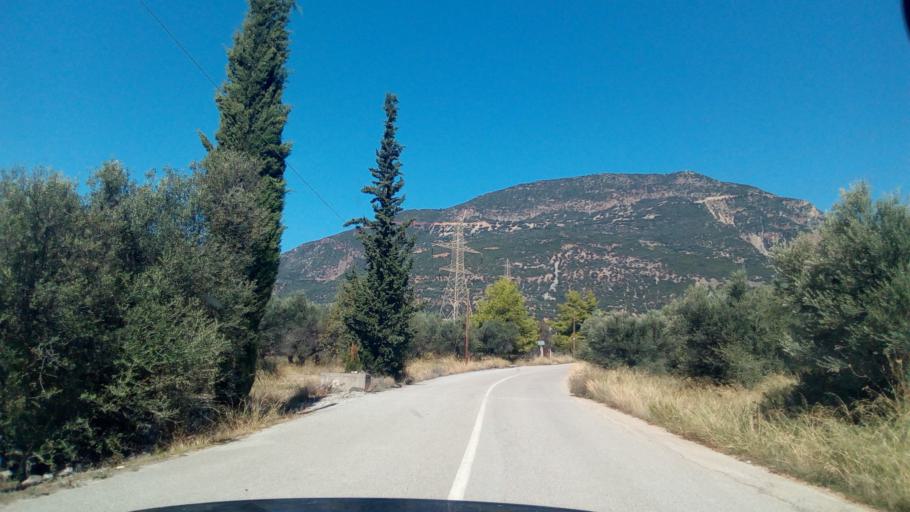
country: GR
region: West Greece
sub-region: Nomos Achaias
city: Selianitika
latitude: 38.3777
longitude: 22.0936
